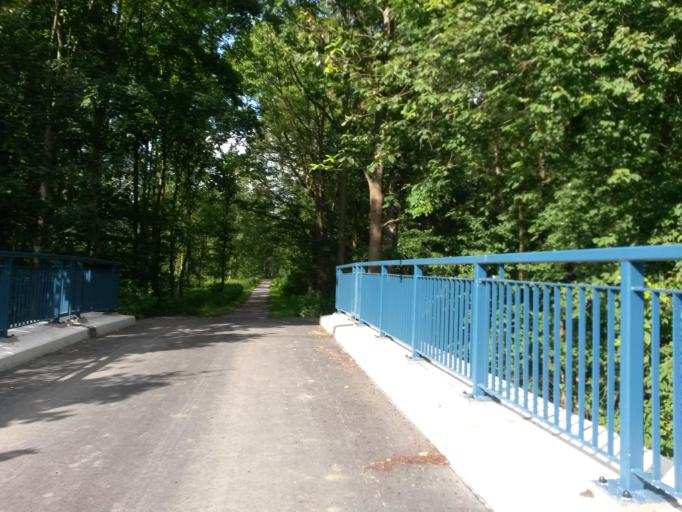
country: CZ
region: Olomoucky
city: Litovel
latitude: 49.6981
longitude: 17.1165
